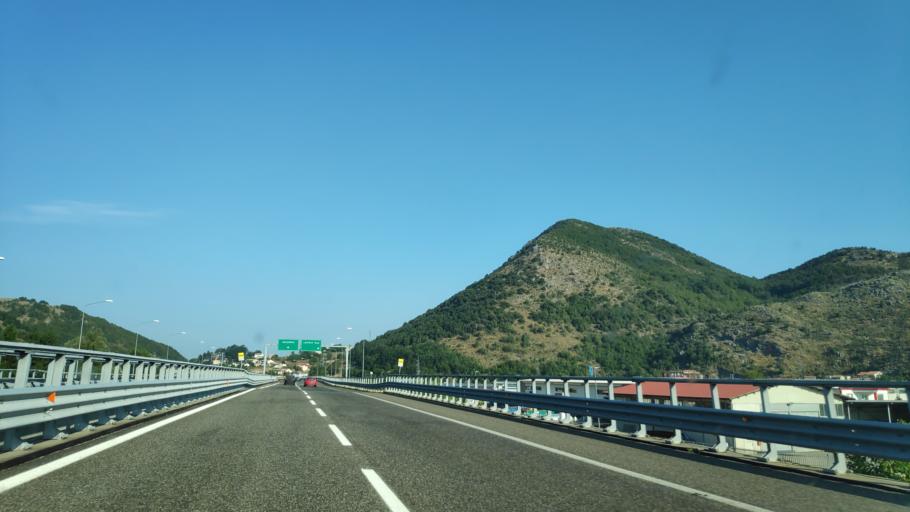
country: IT
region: Basilicate
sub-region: Provincia di Potenza
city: Lauria
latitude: 40.0157
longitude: 15.8942
